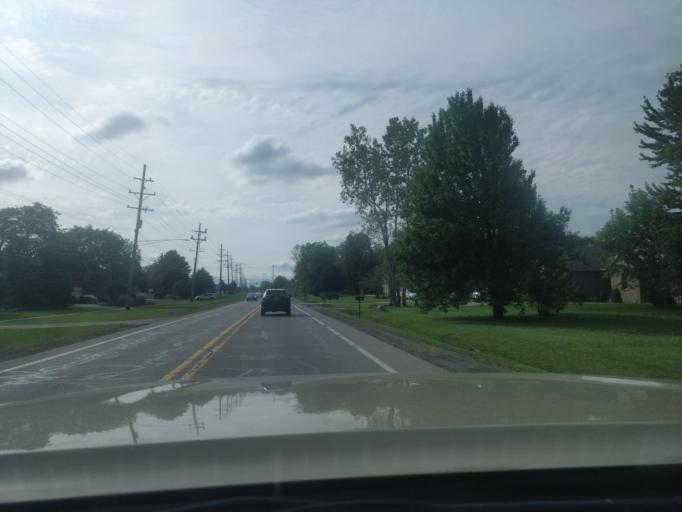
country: US
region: Michigan
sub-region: Wayne County
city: Woodhaven
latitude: 42.1541
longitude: -83.2489
